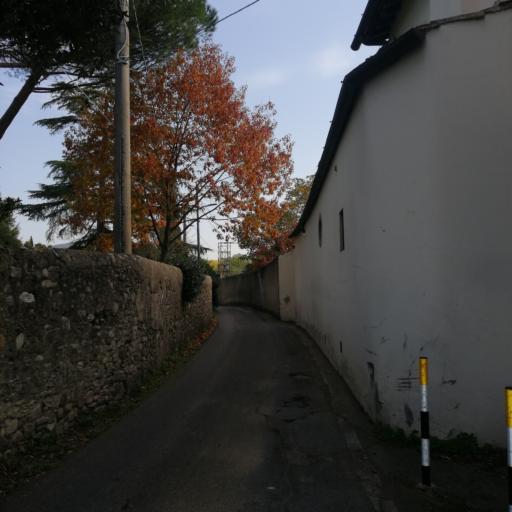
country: IT
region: Tuscany
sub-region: Province of Florence
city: Bagno a Ripoli
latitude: 43.7595
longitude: 11.3149
